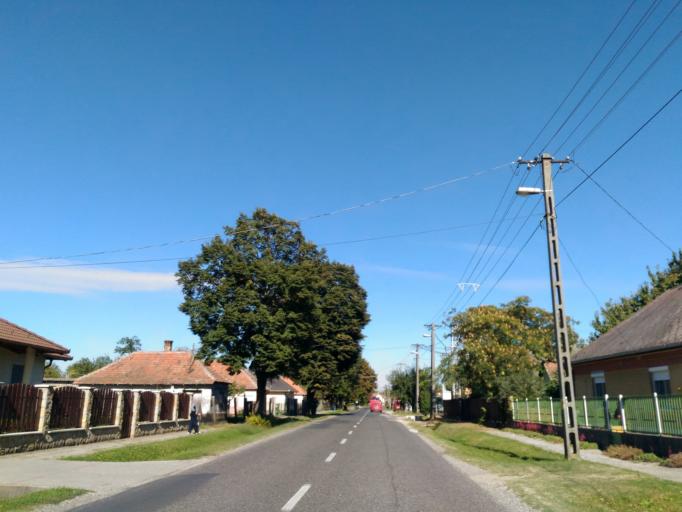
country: HU
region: Fejer
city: Ivancsa
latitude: 47.1409
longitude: 18.8354
